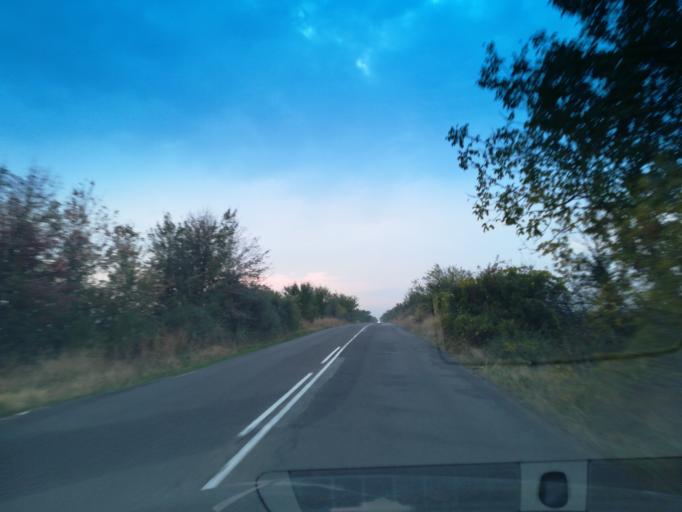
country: BG
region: Stara Zagora
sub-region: Obshtina Chirpan
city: Chirpan
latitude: 42.1929
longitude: 25.2978
